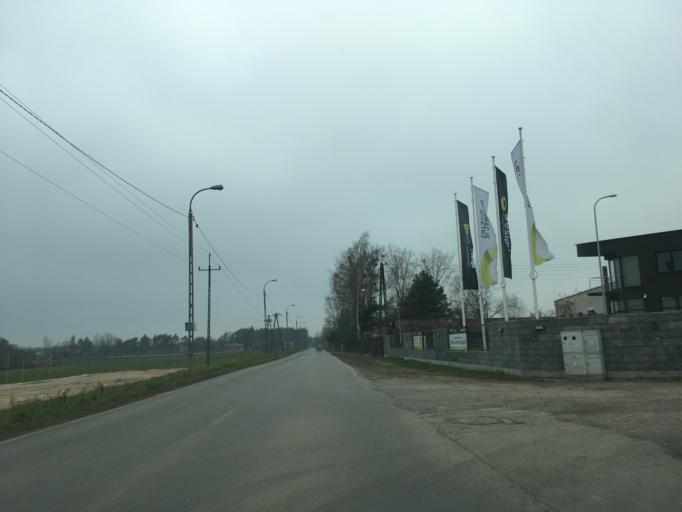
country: PL
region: Masovian Voivodeship
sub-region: Powiat piaseczynski
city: Lesznowola
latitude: 52.0696
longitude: 20.9408
